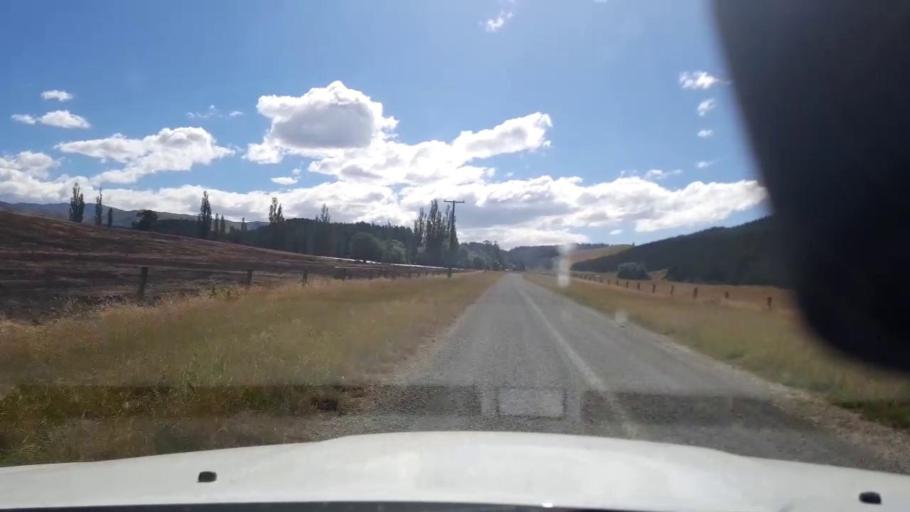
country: NZ
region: Canterbury
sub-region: Timaru District
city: Pleasant Point
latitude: -44.3142
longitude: 170.9254
